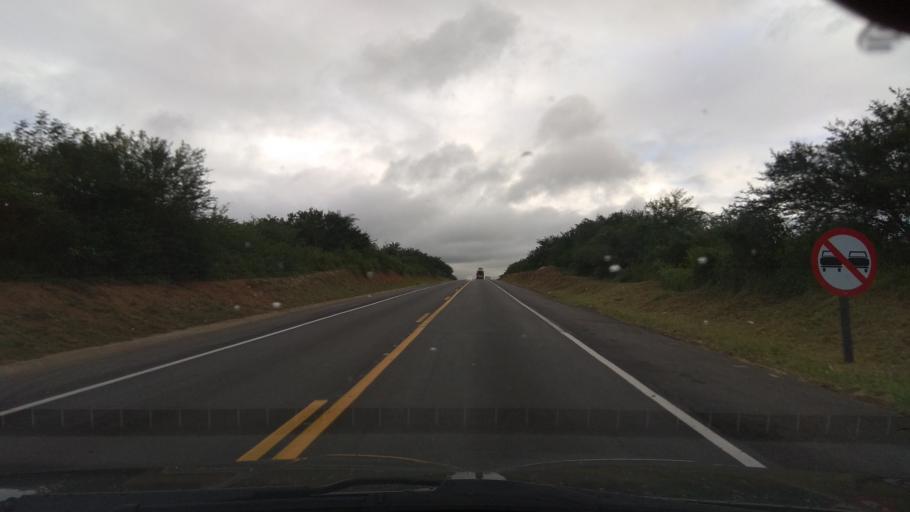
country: BR
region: Bahia
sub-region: Santa Ines
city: Santa Ines
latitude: -13.2834
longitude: -40.0189
